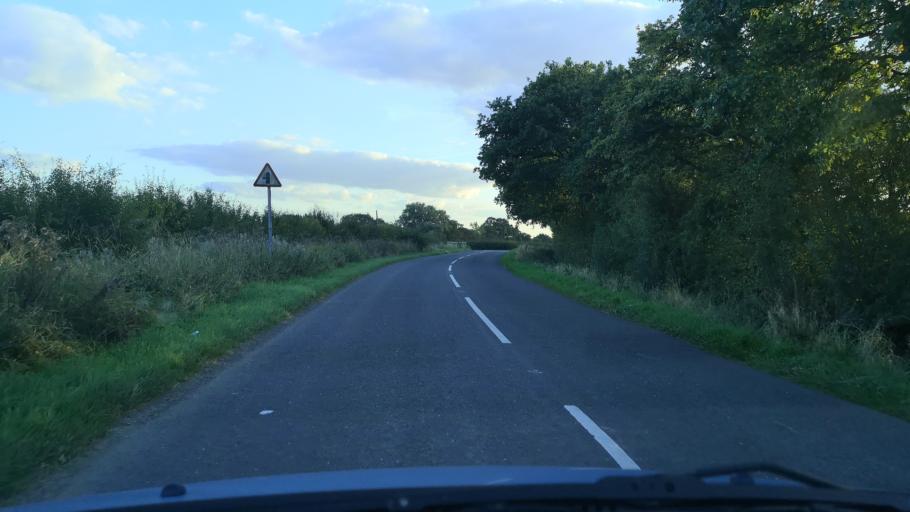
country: GB
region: England
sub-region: Doncaster
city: Moss
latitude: 53.6213
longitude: -1.0742
